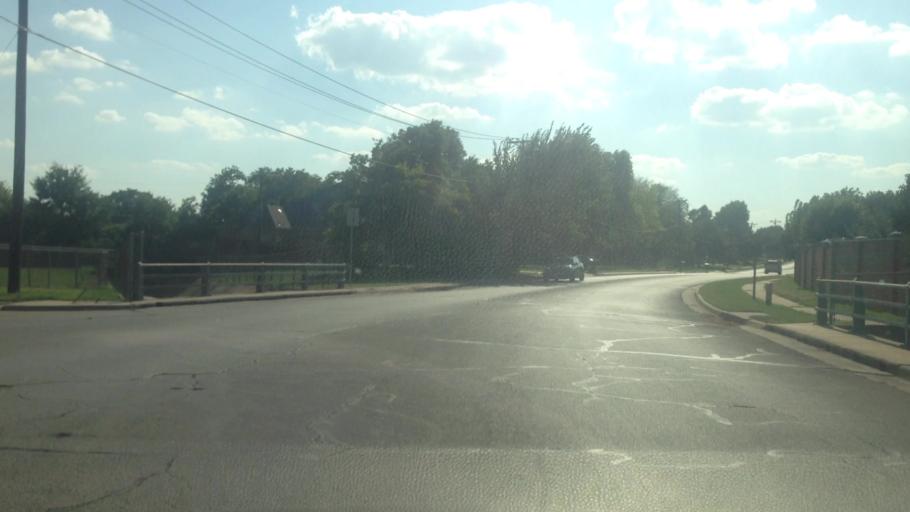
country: US
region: Texas
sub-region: Tarrant County
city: North Richland Hills
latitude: 32.8677
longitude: -97.2151
